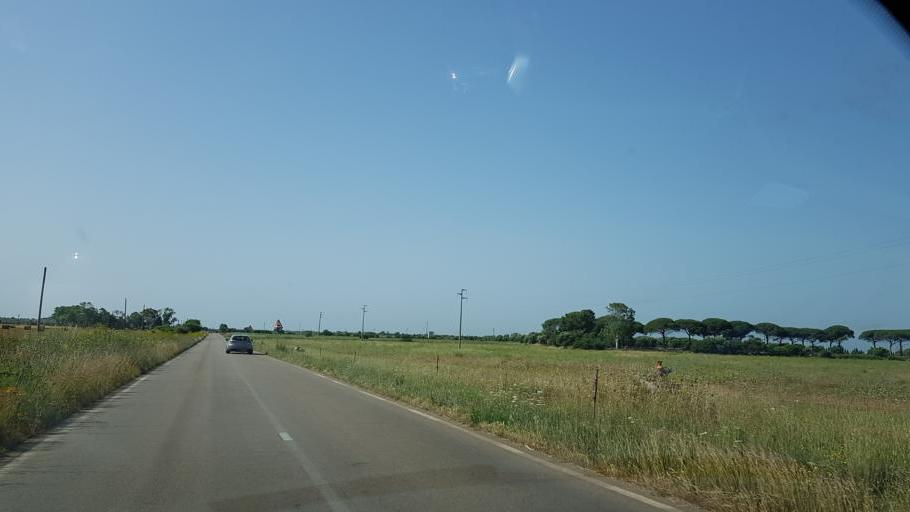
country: IT
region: Apulia
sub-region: Provincia di Brindisi
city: San Pancrazio Salentino
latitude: 40.3426
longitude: 17.8482
